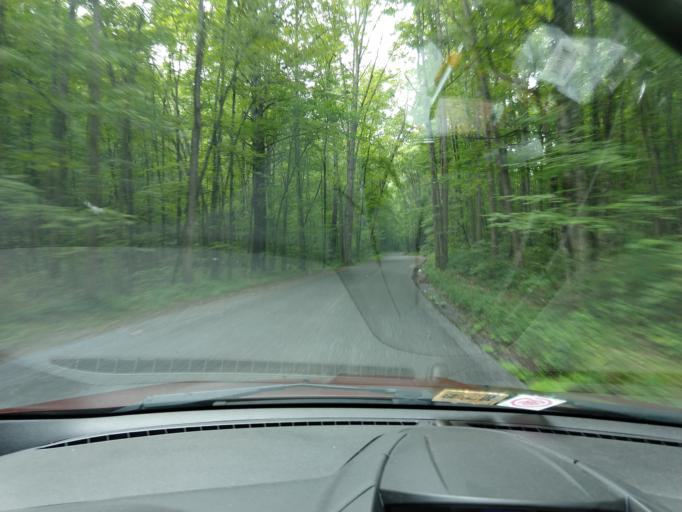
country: US
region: Virginia
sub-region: City of Covington
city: Covington
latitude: 37.9232
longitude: -80.0748
